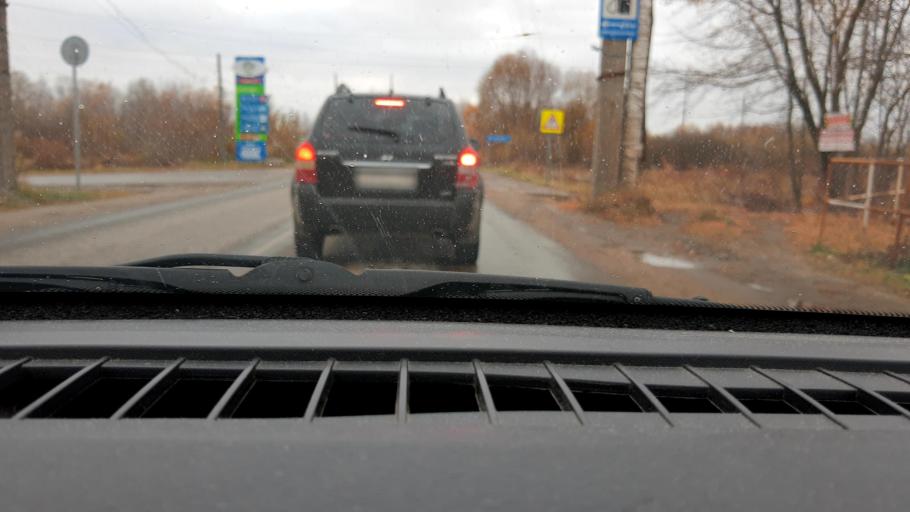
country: RU
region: Nizjnij Novgorod
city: Kstovo
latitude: 56.1176
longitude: 44.1497
